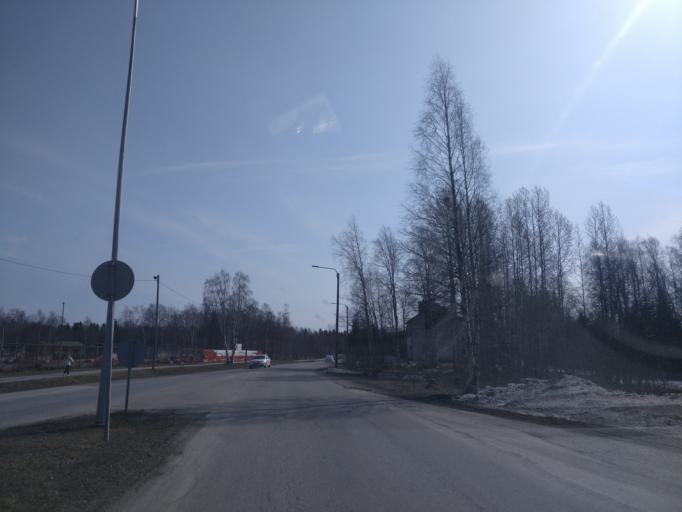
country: FI
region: Lapland
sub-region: Kemi-Tornio
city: Kemi
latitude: 65.7278
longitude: 24.6129
